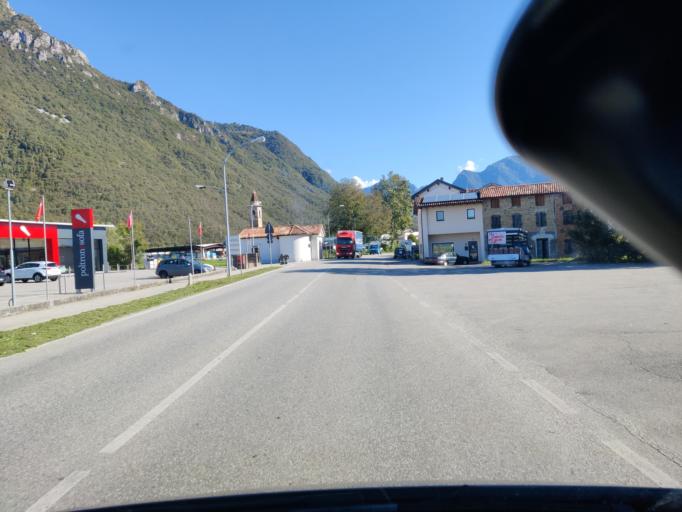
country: IT
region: Veneto
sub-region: Provincia di Belluno
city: Belluno
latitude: 46.1666
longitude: 12.2454
